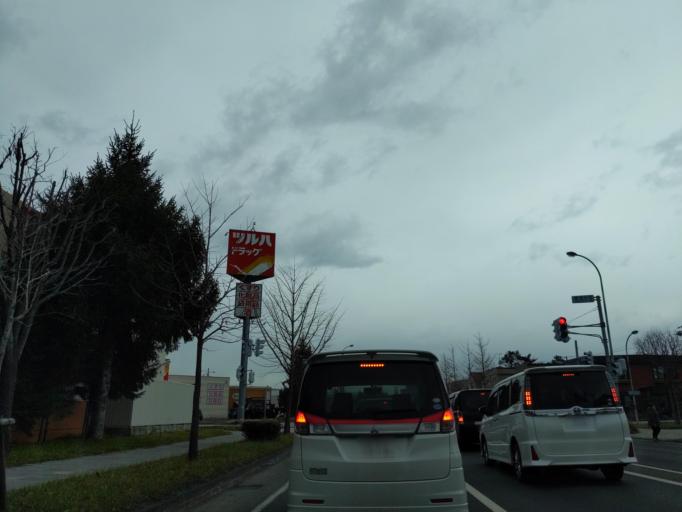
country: JP
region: Hokkaido
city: Sapporo
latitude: 43.1434
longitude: 141.3724
